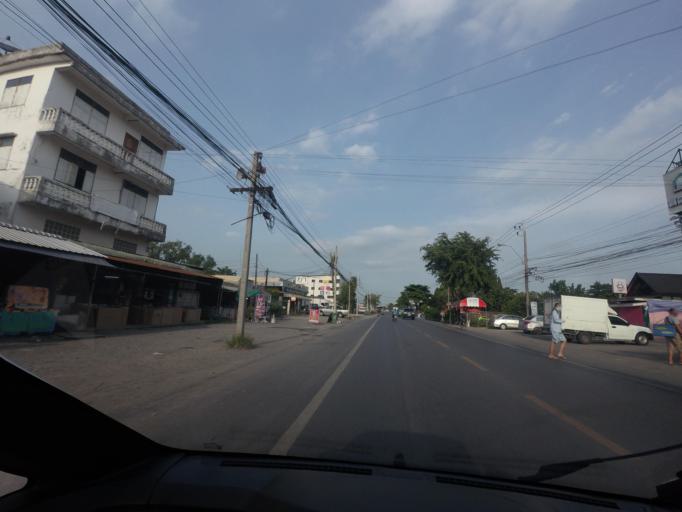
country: TH
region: Bangkok
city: Nong Chok
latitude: 13.8515
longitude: 100.8788
